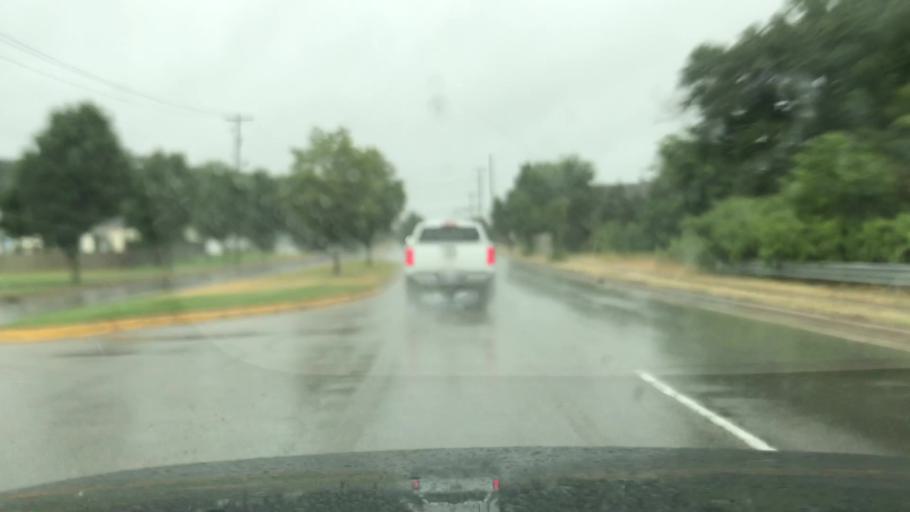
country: US
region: Michigan
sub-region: Kent County
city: Wyoming
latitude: 42.8689
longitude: -85.7234
